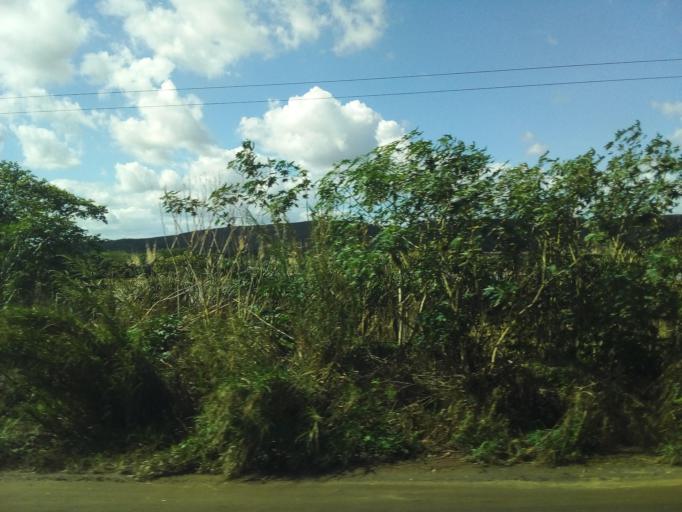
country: BR
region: Minas Gerais
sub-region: Governador Valadares
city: Governador Valadares
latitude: -18.8685
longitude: -41.7714
